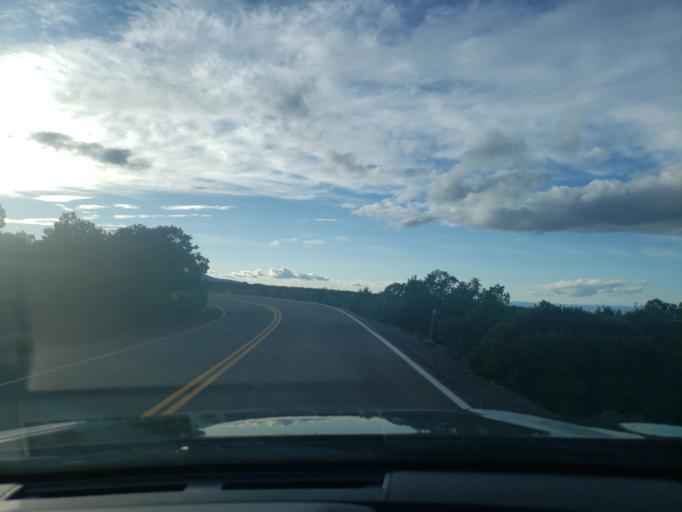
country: US
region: Colorado
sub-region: Mesa County
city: Redlands
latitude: 39.0327
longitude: -108.6607
